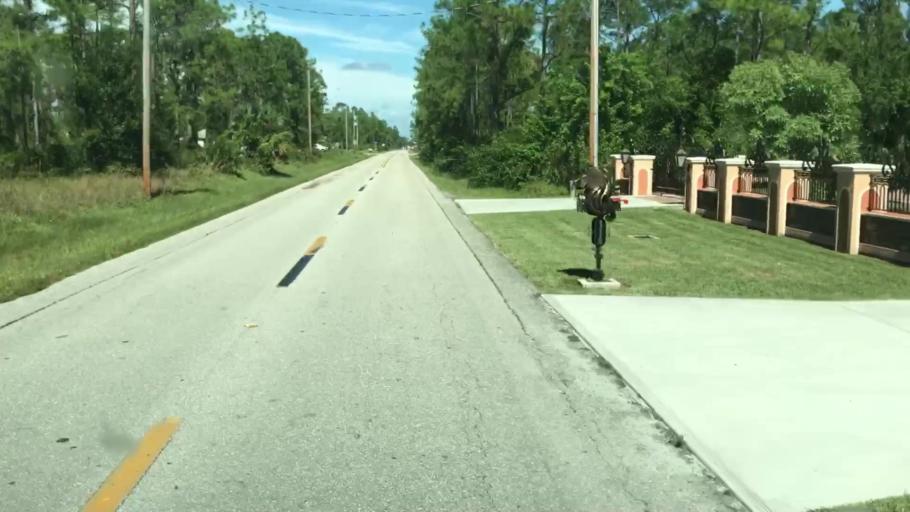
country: US
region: Florida
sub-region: Lee County
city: Lehigh Acres
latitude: 26.6409
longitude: -81.6465
